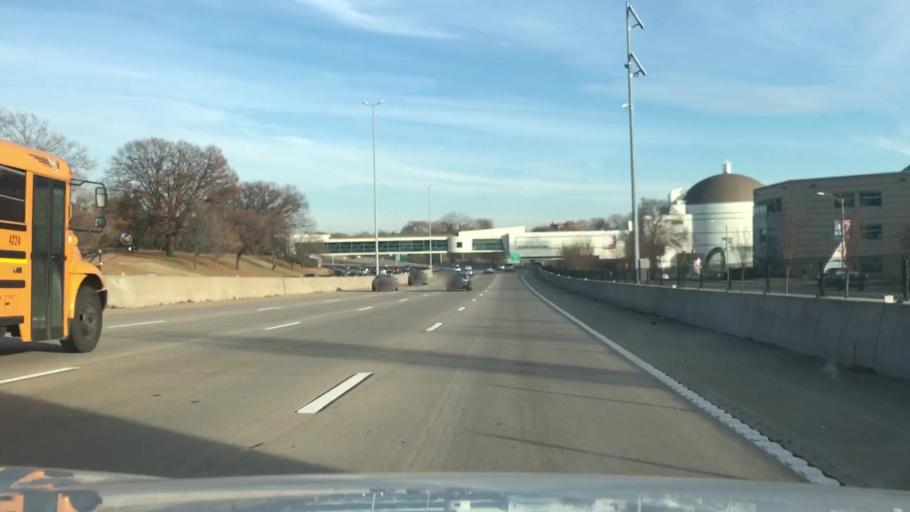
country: US
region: Missouri
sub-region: Saint Louis County
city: University City
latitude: 38.6299
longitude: -90.2735
